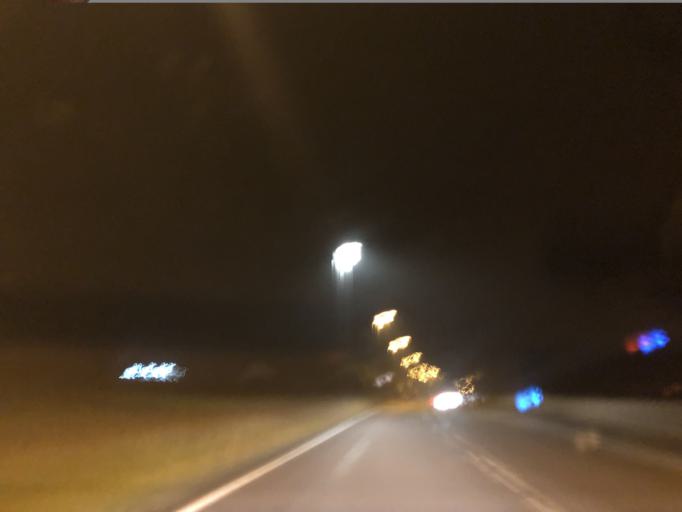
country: GB
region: England
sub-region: Borough of Oldham
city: Shaw
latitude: 53.5756
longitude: -2.0571
